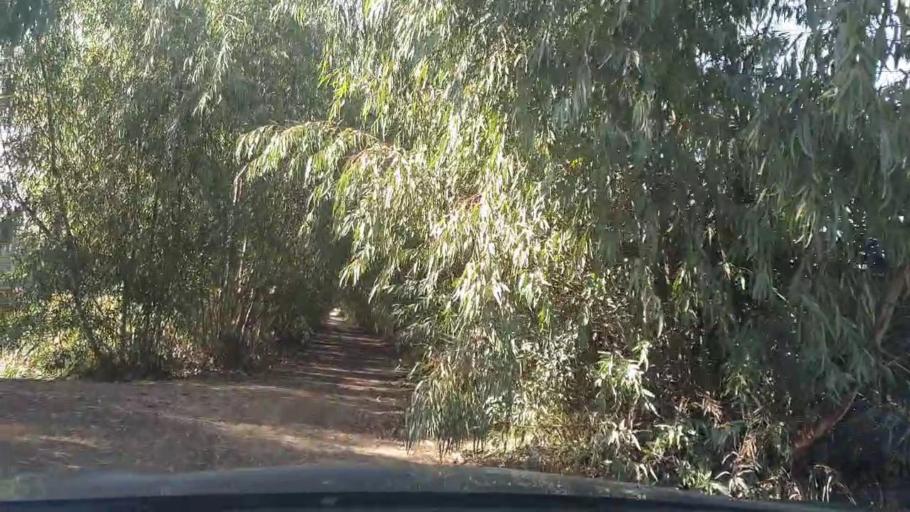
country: PK
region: Sindh
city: Mirpur Mathelo
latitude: 28.1390
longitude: 69.5979
